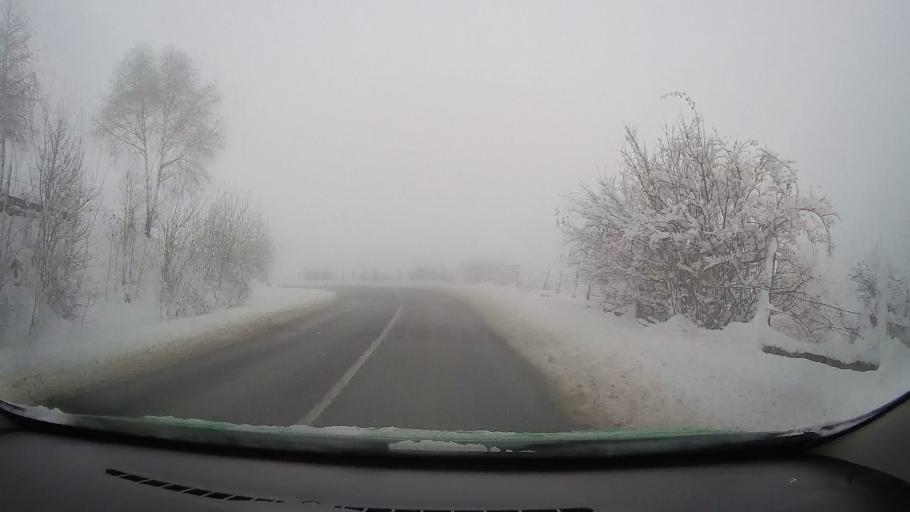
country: RO
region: Sibiu
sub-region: Comuna Jina
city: Jina
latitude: 45.7894
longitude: 23.6946
